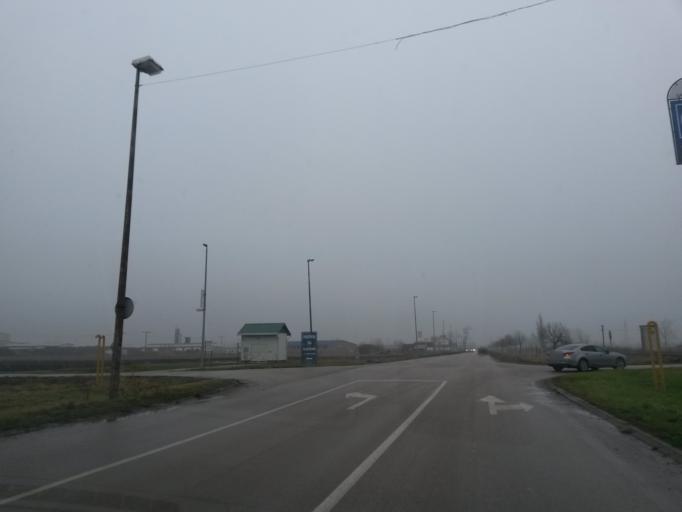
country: HR
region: Vukovarsko-Srijemska
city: Zupanja
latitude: 45.0953
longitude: 18.6976
